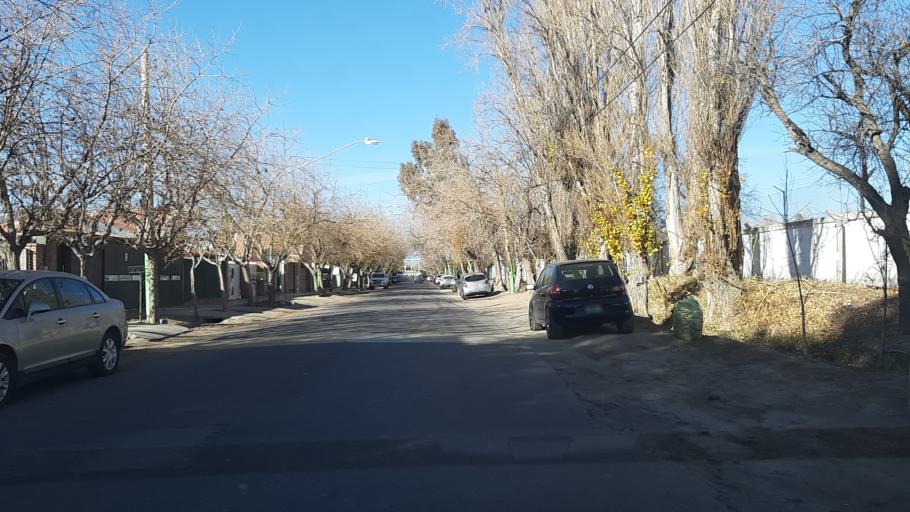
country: AR
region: San Juan
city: San Juan
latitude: -31.5280
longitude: -68.5917
